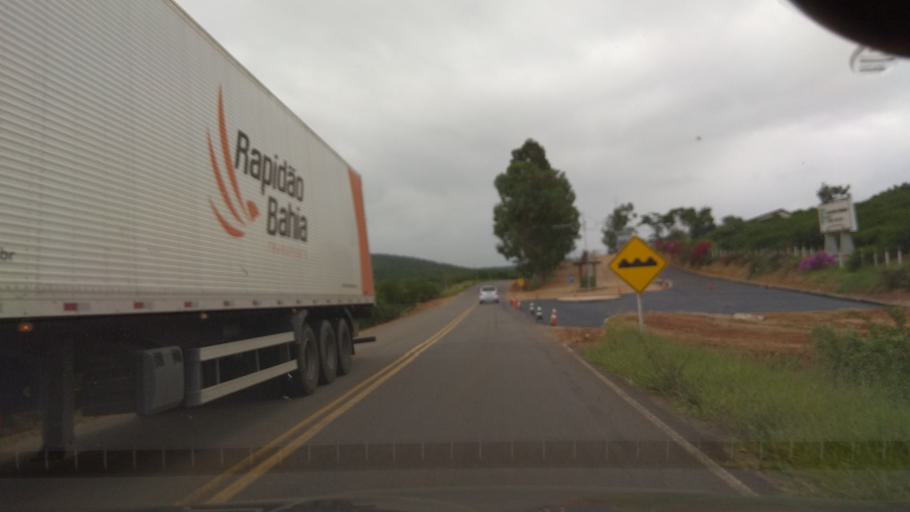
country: BR
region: Bahia
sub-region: Santa Ines
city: Santa Ines
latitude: -13.2733
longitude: -39.8069
